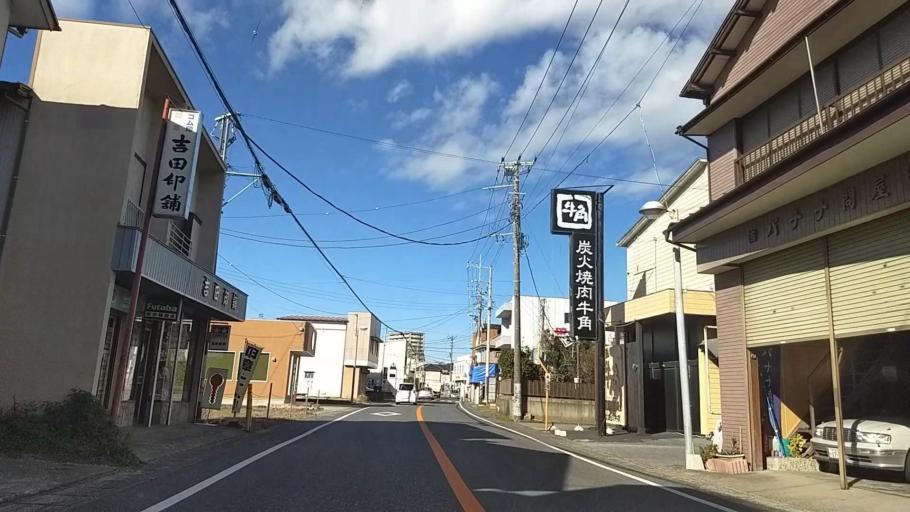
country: JP
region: Chiba
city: Tateyama
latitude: 34.9920
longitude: 139.8674
